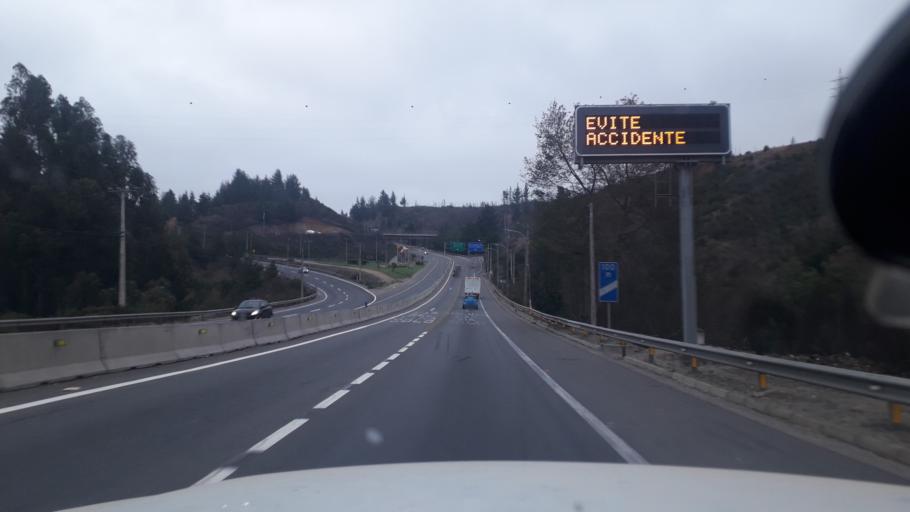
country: CL
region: Valparaiso
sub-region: Provincia de Valparaiso
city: Vina del Mar
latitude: -33.0813
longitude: -71.5464
